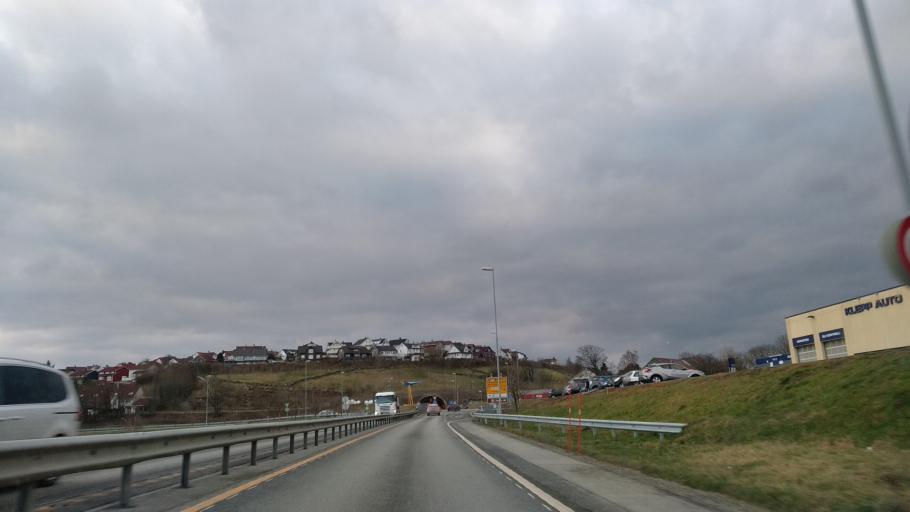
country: NO
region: Rogaland
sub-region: Klepp
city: Kleppe
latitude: 58.7800
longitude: 5.6250
